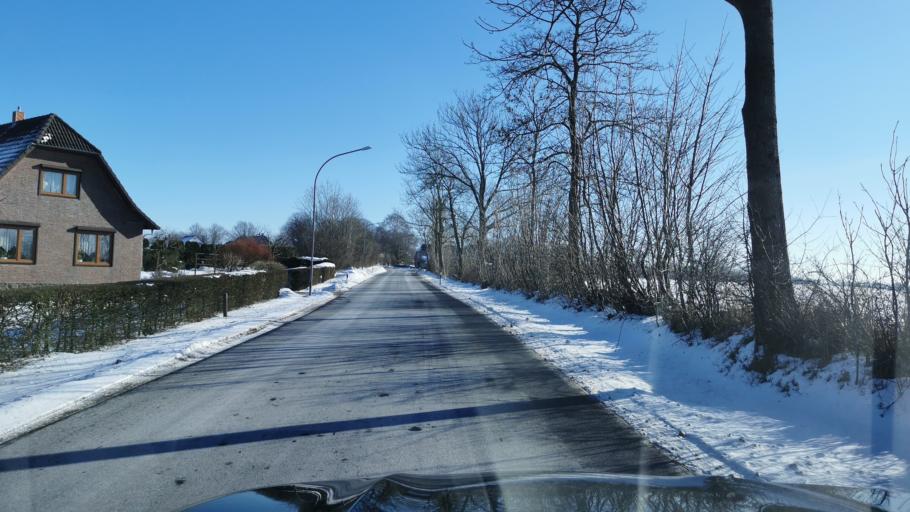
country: DE
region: Schleswig-Holstein
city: Sorup
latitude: 54.7318
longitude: 9.6498
